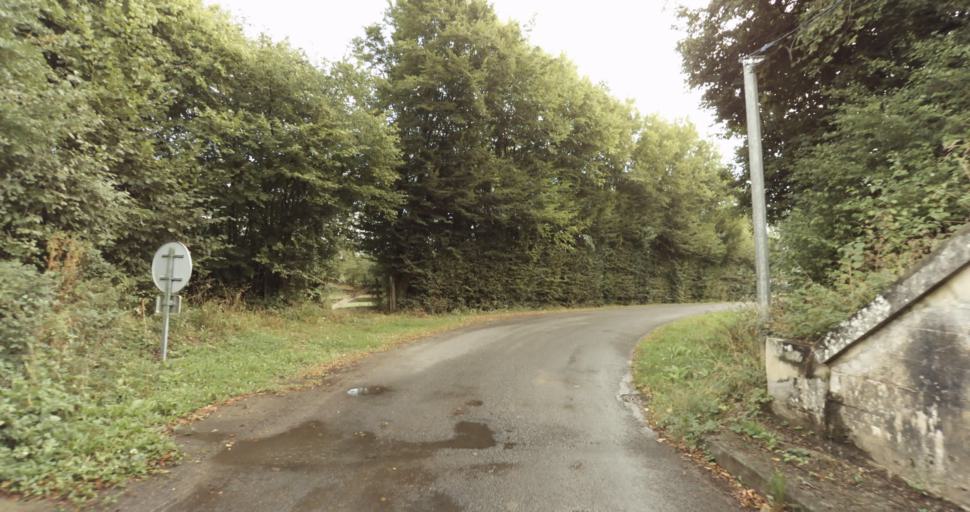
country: FR
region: Lower Normandy
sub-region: Departement de l'Orne
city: Sainte-Gauburge-Sainte-Colombe
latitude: 48.7079
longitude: 0.3714
